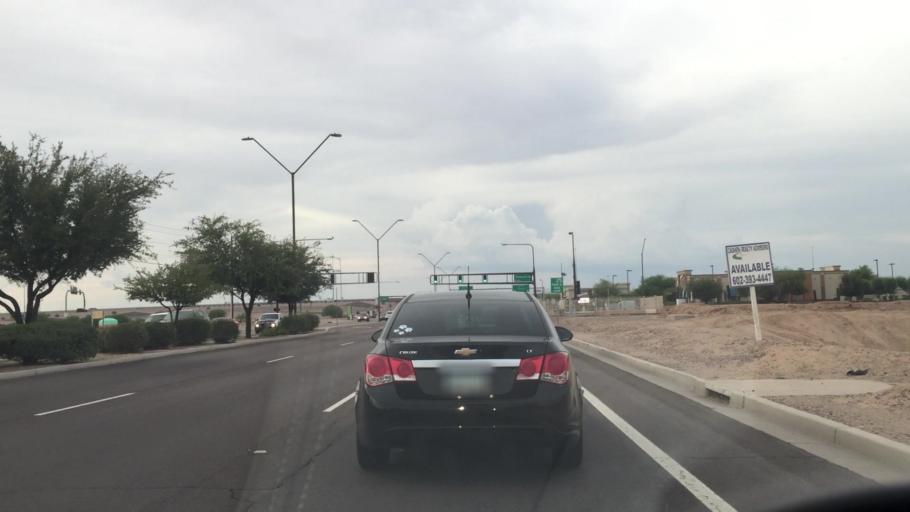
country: US
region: Arizona
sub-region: Maricopa County
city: Tolleson
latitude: 33.4556
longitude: -112.3064
